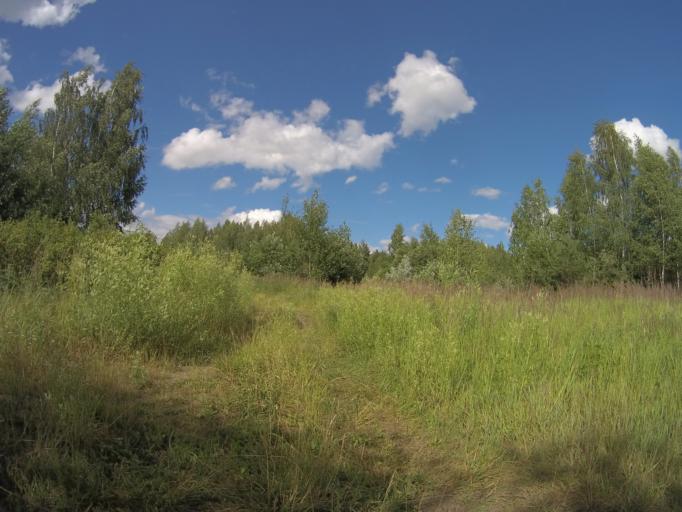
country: RU
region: Vladimir
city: Vladimir
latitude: 56.0891
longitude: 40.3836
